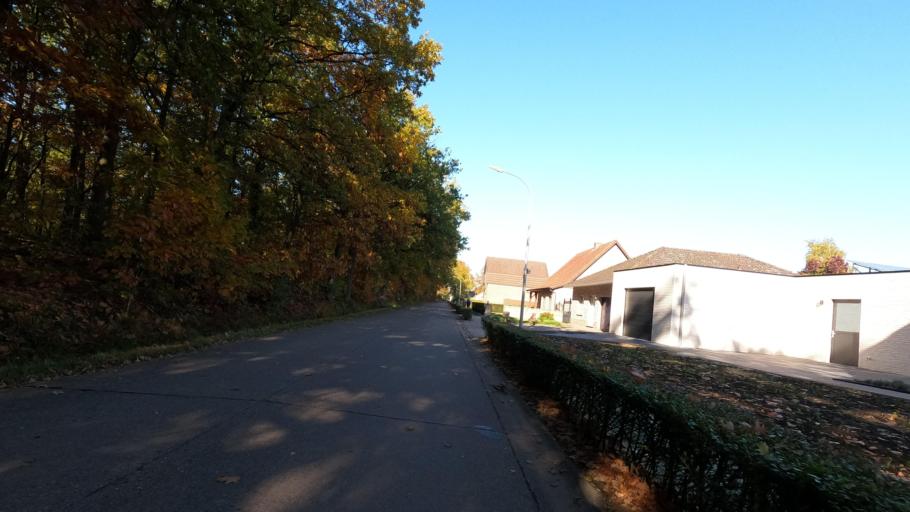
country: BE
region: Flanders
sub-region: Provincie Antwerpen
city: Merksplas
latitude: 51.3548
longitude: 4.8437
